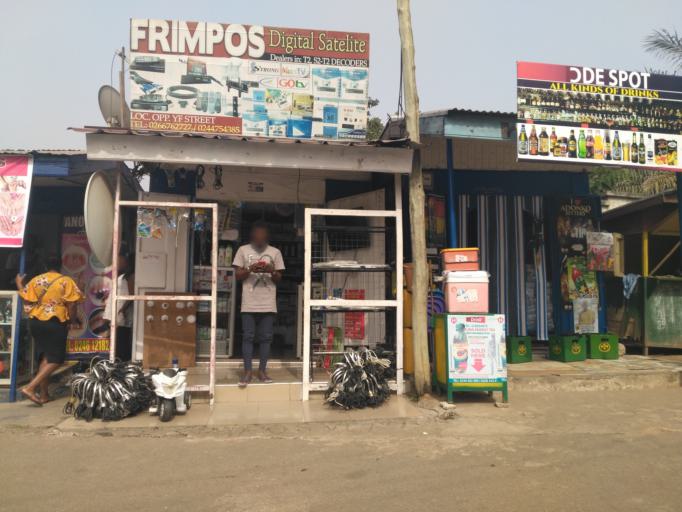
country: GH
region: Ashanti
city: Kumasi
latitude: 6.6834
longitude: -1.6078
